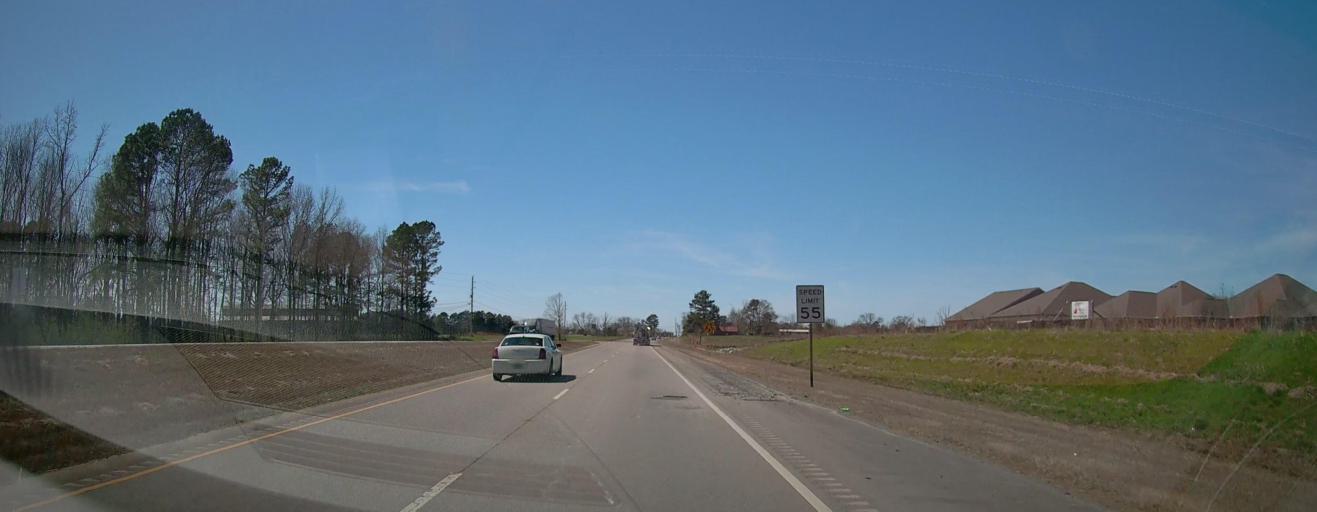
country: US
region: Alabama
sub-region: Cullman County
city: Cullman
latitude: 34.1779
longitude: -86.7356
